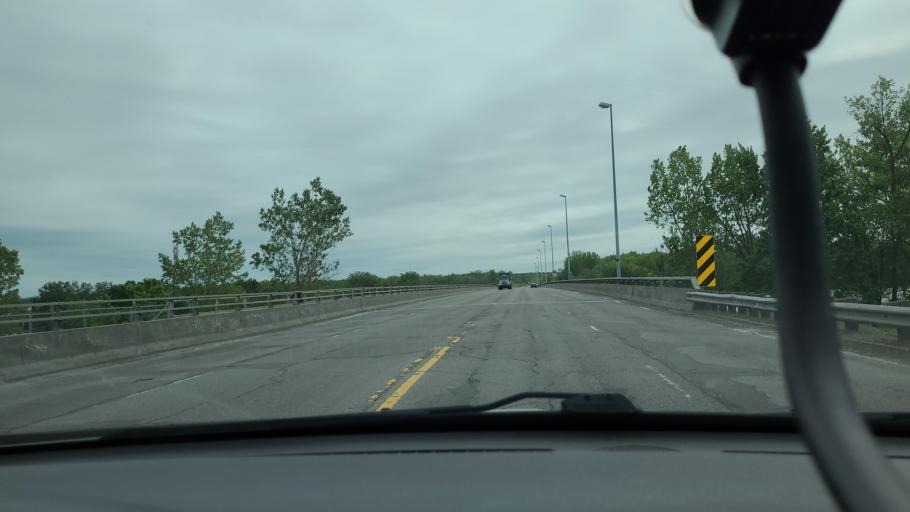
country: CA
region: Quebec
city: Bois-des-Filion
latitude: 45.6627
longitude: -73.7554
